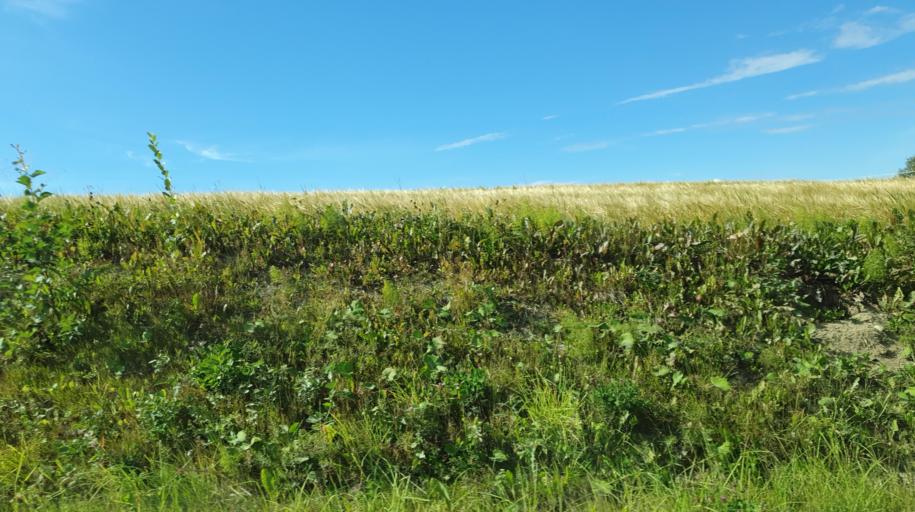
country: NO
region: Nord-Trondelag
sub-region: Levanger
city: Skogn
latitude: 63.6987
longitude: 11.2374
